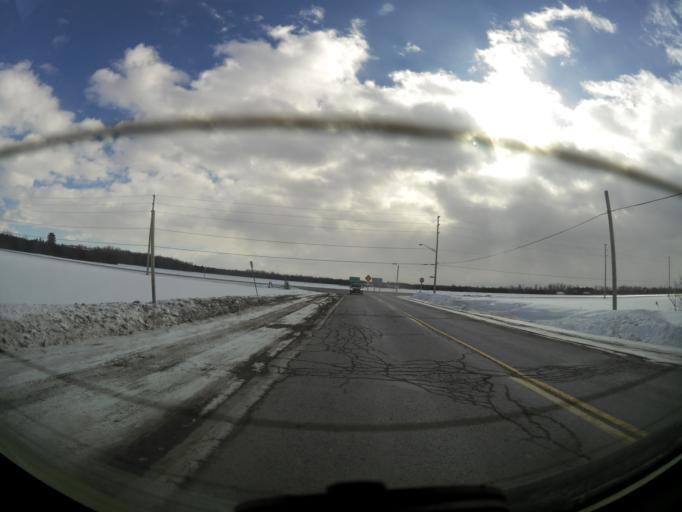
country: CA
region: Ontario
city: Ottawa
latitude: 45.3075
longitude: -75.5053
